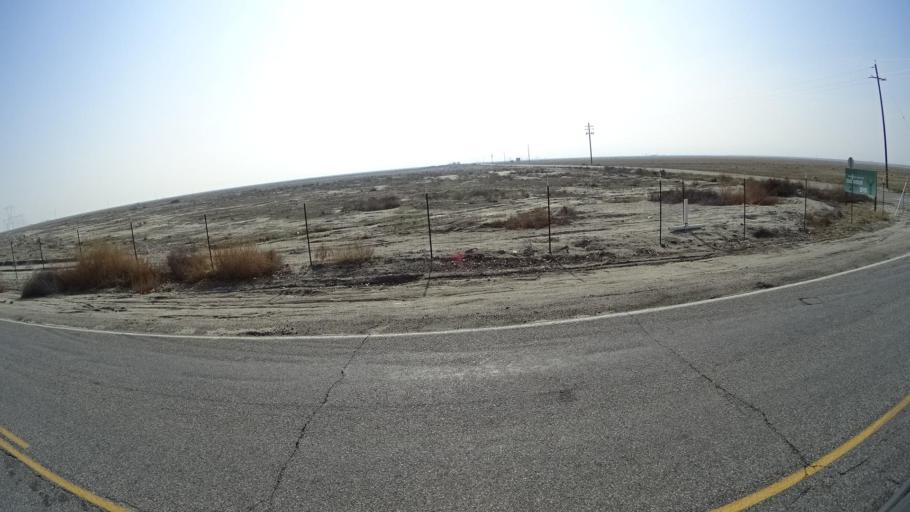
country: US
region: California
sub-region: Kern County
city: Buttonwillow
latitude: 35.3549
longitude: -119.3588
